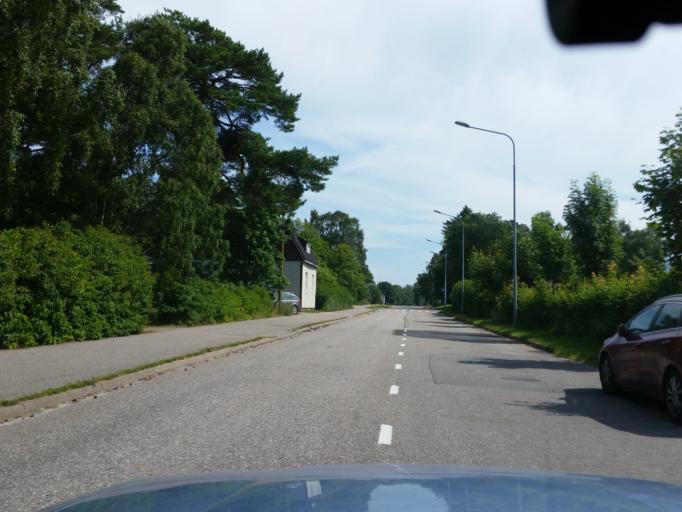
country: FI
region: Uusimaa
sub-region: Raaseporin
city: Hanko
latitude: 59.8339
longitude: 22.9472
